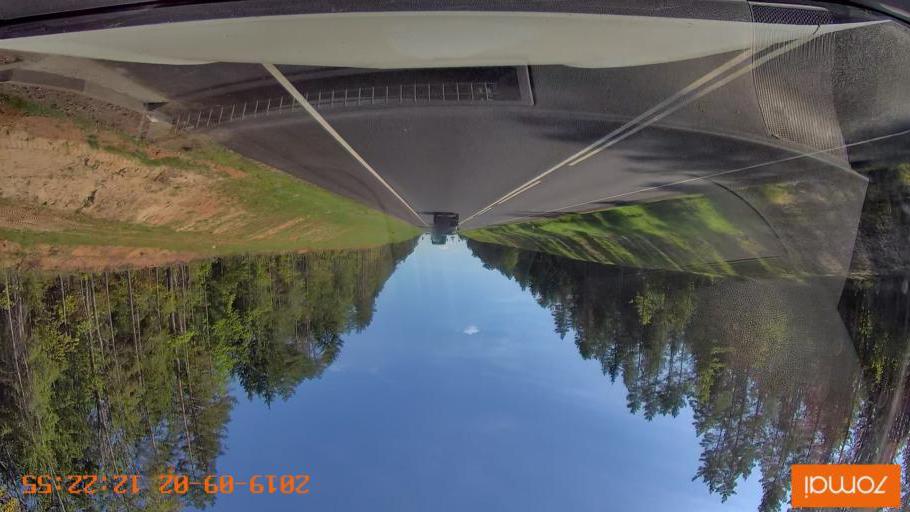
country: RU
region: Smolensk
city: Shumyachi
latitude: 53.8778
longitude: 32.6265
